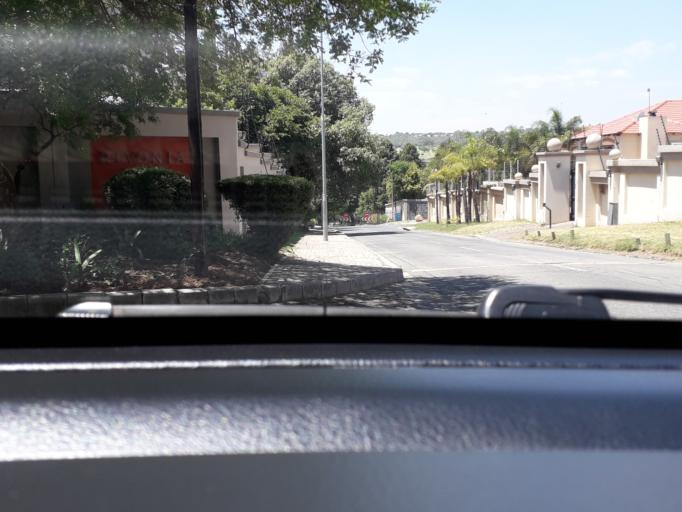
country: ZA
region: Gauteng
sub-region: City of Johannesburg Metropolitan Municipality
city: Midrand
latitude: -26.0514
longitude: 28.0621
